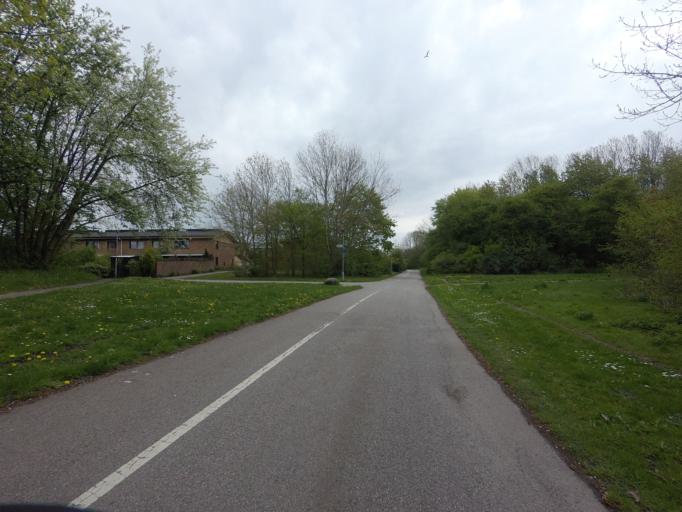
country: SE
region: Skane
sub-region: Malmo
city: Tygelsjo
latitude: 55.5532
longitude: 13.0144
